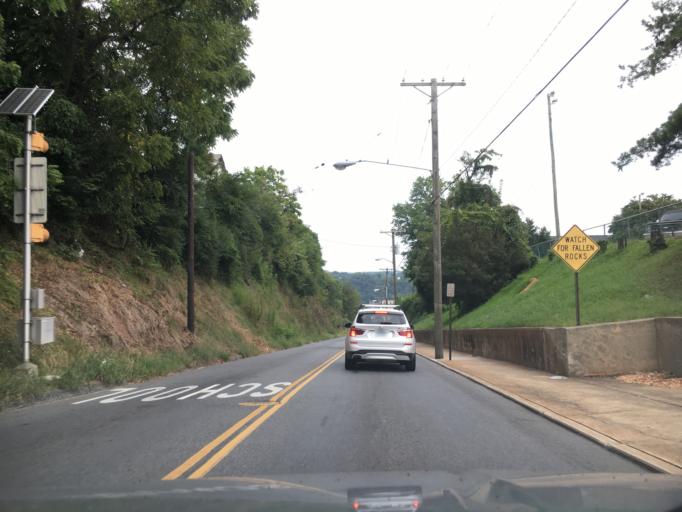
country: US
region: Virginia
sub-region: City of Lynchburg
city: Lynchburg
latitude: 37.4084
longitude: -79.1473
